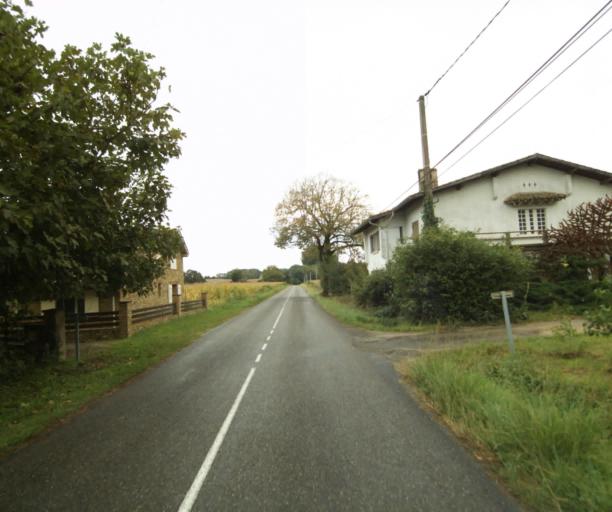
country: FR
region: Midi-Pyrenees
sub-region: Departement du Gers
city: Cazaubon
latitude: 43.8664
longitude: -0.0797
